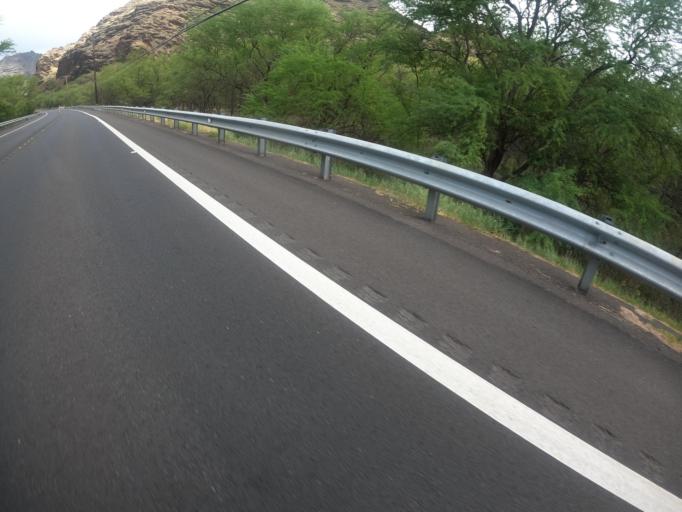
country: US
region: Hawaii
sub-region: Honolulu County
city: Makaha Valley
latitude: 21.5137
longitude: -158.2280
